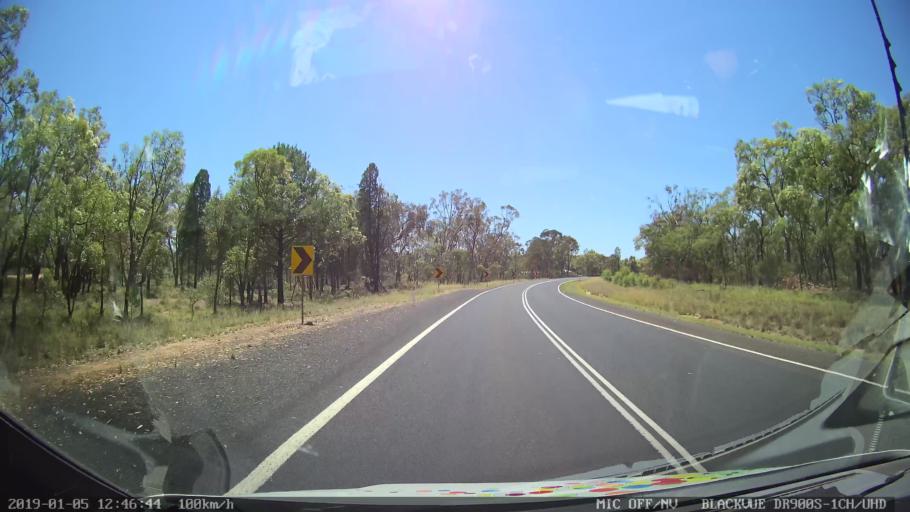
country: AU
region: New South Wales
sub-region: Warrumbungle Shire
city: Coonabarabran
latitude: -31.1150
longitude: 149.5666
